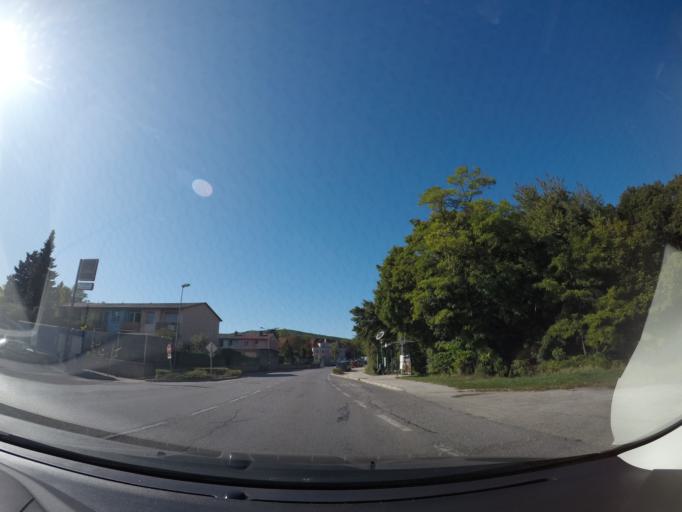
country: AT
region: Lower Austria
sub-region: Politischer Bezirk Modling
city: Kaltenleutgeben
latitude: 48.1385
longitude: 16.2044
